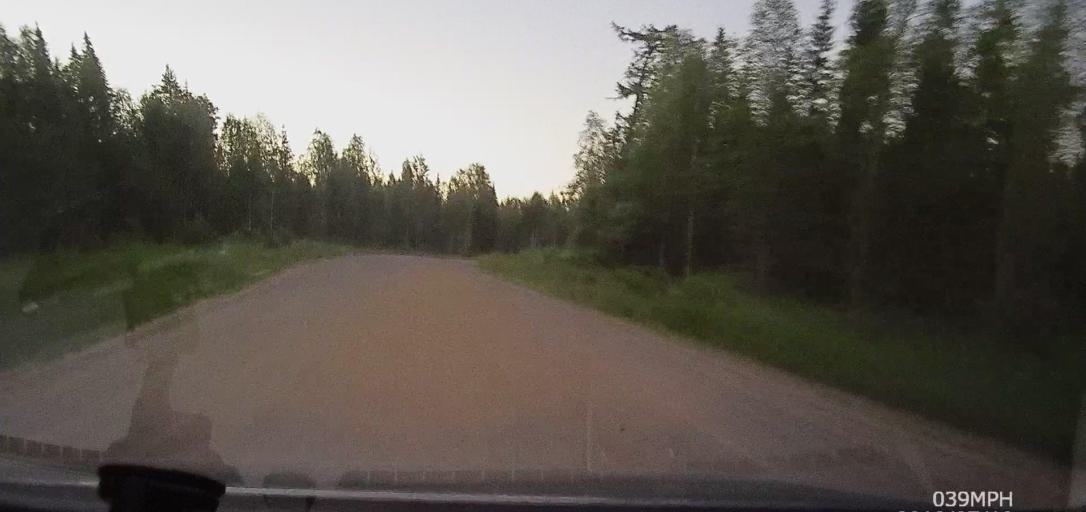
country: RU
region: Arkhangelskaya
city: Pinega
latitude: 64.4333
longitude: 43.1350
